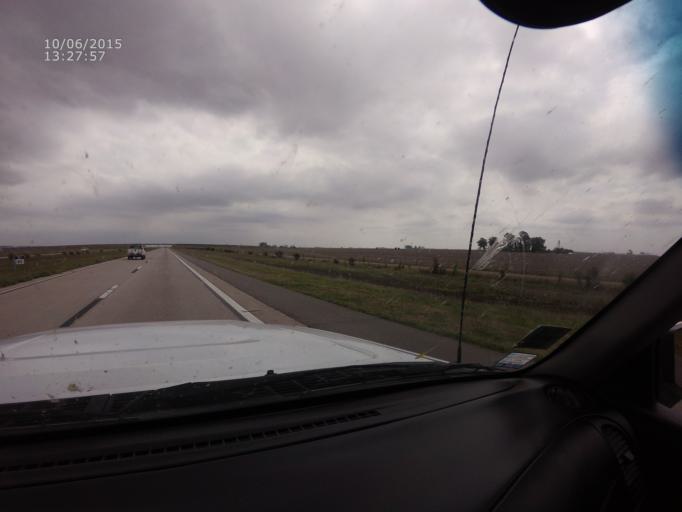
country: AR
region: Cordoba
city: Leones
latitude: -32.6439
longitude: -62.2132
